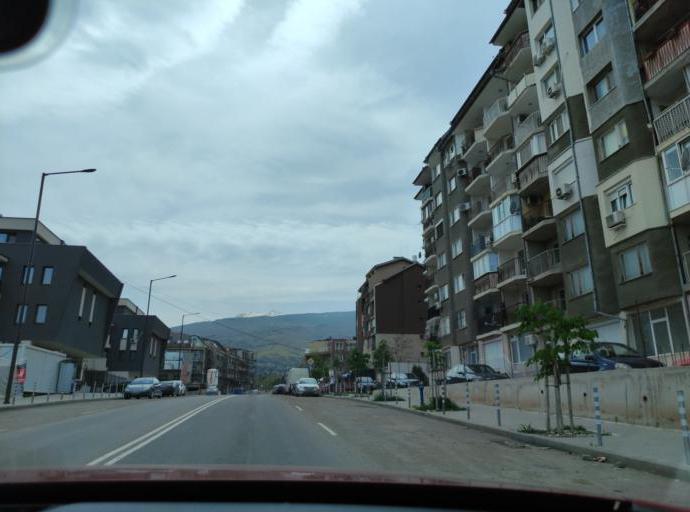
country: BG
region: Sofia-Capital
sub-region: Stolichna Obshtina
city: Sofia
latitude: 42.6375
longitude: 23.3414
